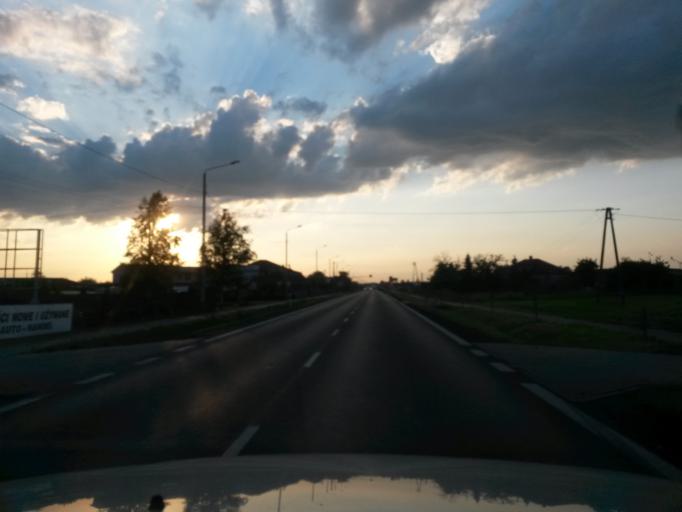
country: PL
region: Lodz Voivodeship
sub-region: Powiat wielunski
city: Wielun
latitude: 51.2352
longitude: 18.5361
